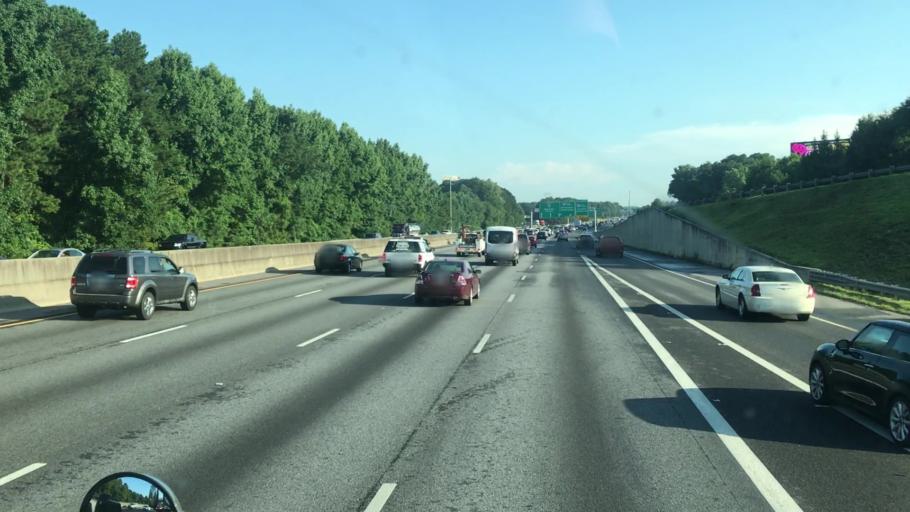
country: US
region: Georgia
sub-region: Clayton County
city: Forest Park
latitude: 33.6187
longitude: -84.3984
